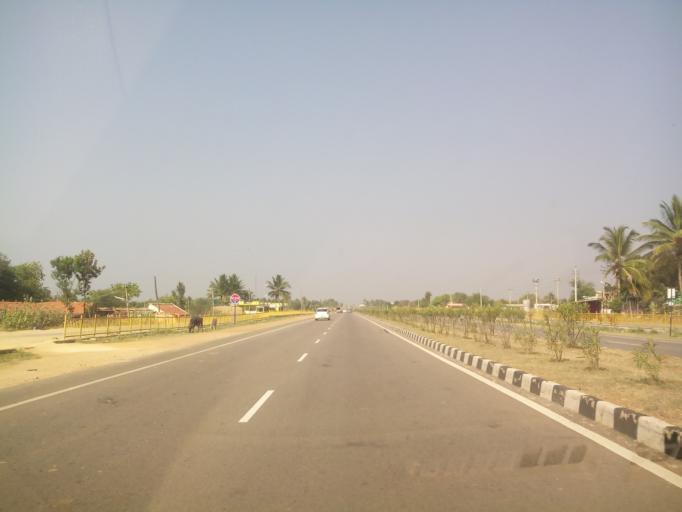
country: IN
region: Karnataka
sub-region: Tumkur
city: Kunigal
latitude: 12.9930
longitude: 76.8937
